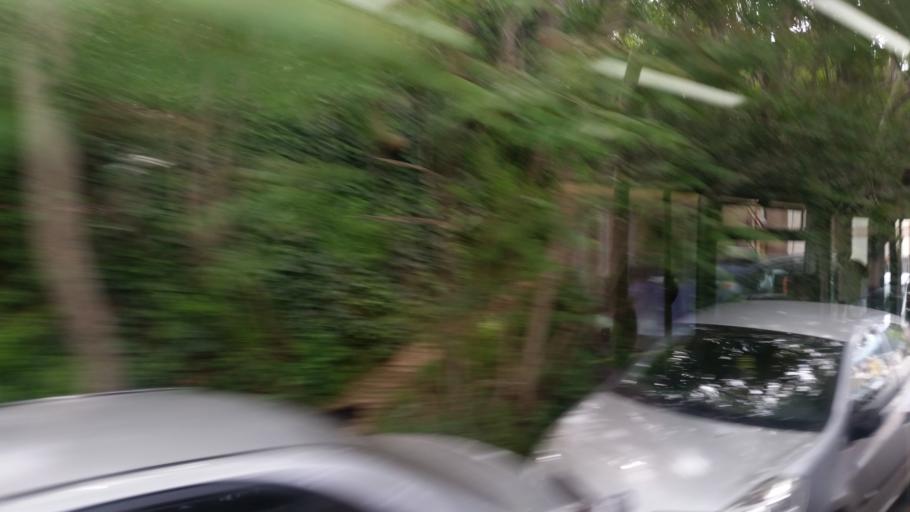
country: ES
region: Catalonia
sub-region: Provincia de Barcelona
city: Horta-Guinardo
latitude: 41.4206
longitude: 2.1623
